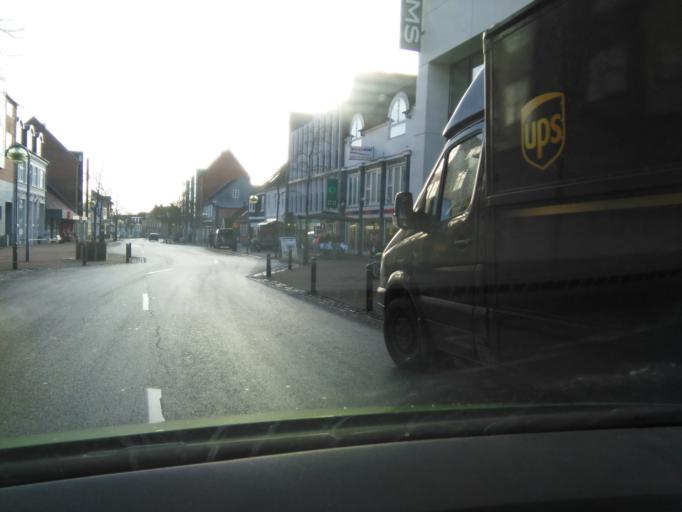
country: DK
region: Central Jutland
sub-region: Skanderborg Kommune
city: Skanderborg
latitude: 56.0336
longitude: 9.9320
